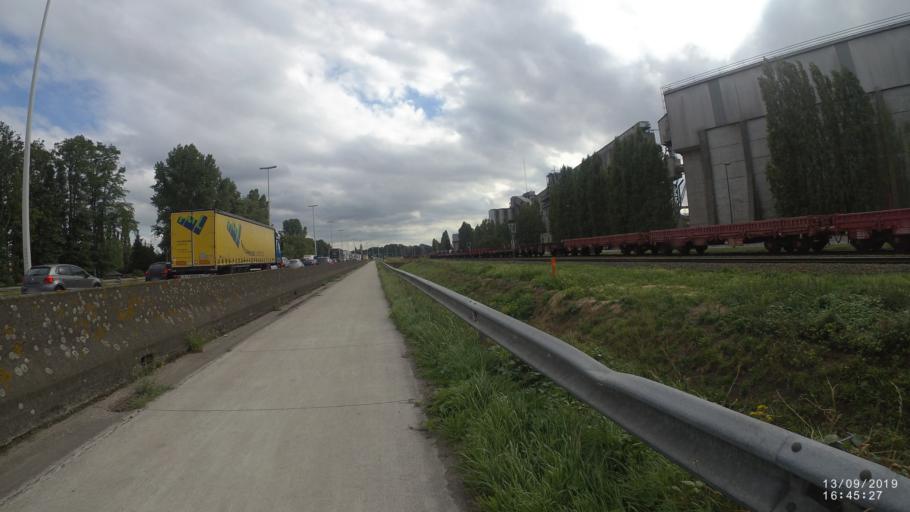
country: BE
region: Flanders
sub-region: Provincie Oost-Vlaanderen
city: Destelbergen
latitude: 51.0921
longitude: 3.7563
